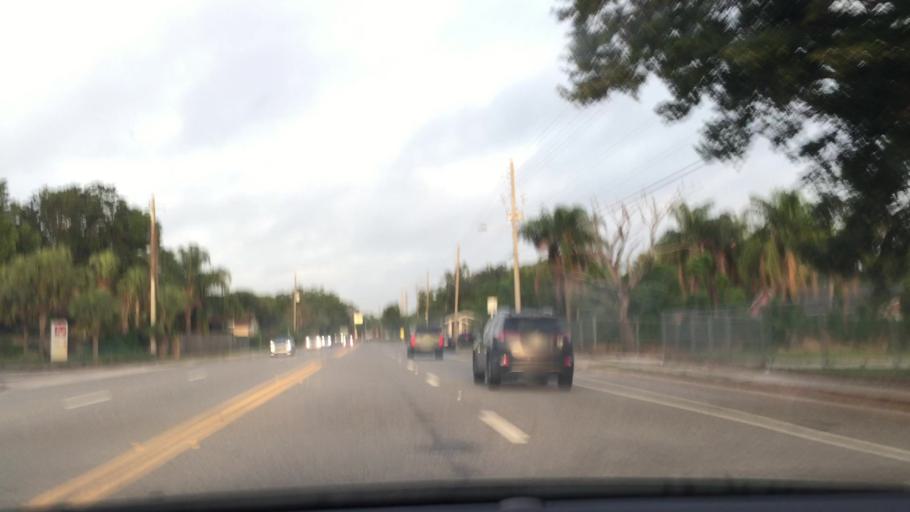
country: US
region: Florida
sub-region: Orange County
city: Fairview Shores
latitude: 28.5835
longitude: -81.3932
